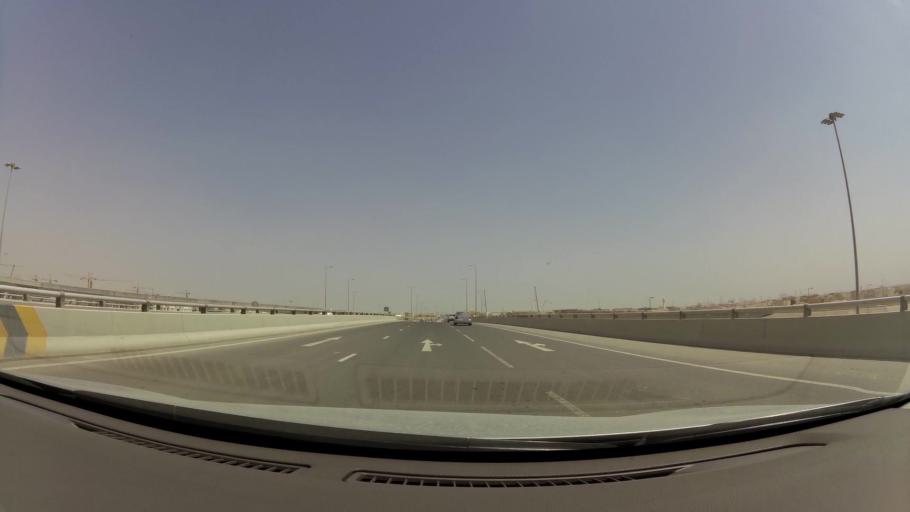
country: QA
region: Baladiyat Umm Salal
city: Umm Salal Muhammad
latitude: 25.4010
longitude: 51.4296
